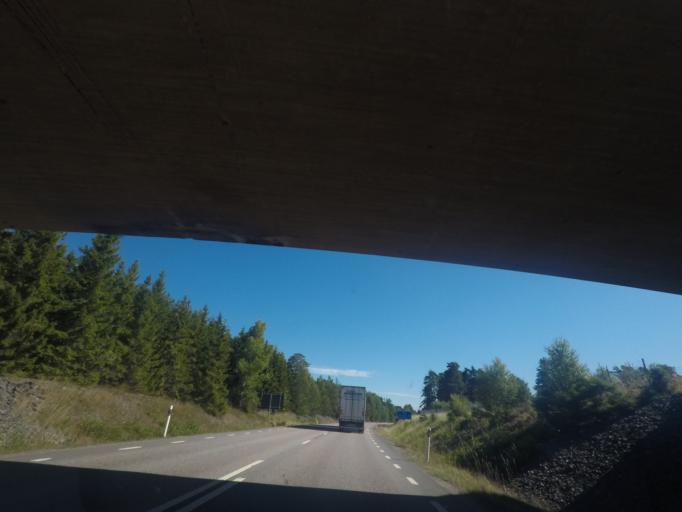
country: SE
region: Soedermanland
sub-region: Strangnas Kommun
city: Strangnas
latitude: 59.3900
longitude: 16.9917
